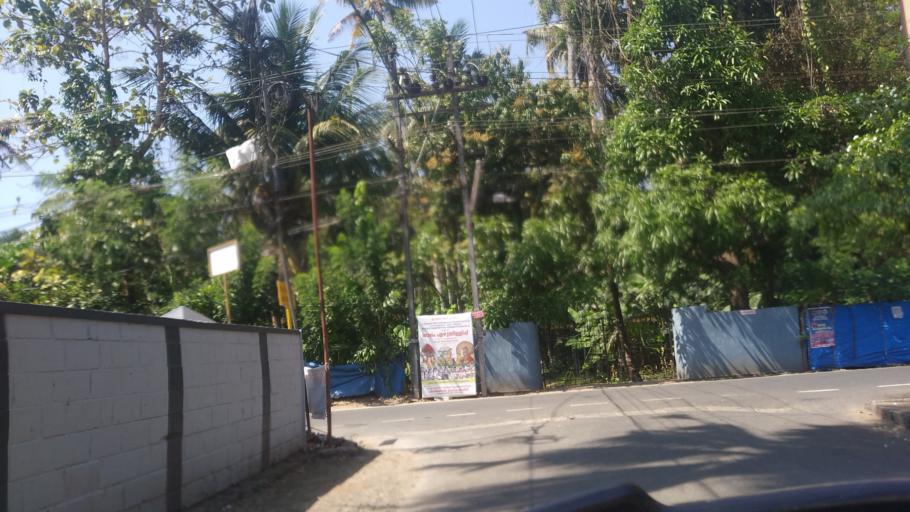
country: IN
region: Kerala
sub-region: Ernakulam
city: Elur
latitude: 10.1350
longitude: 76.2259
